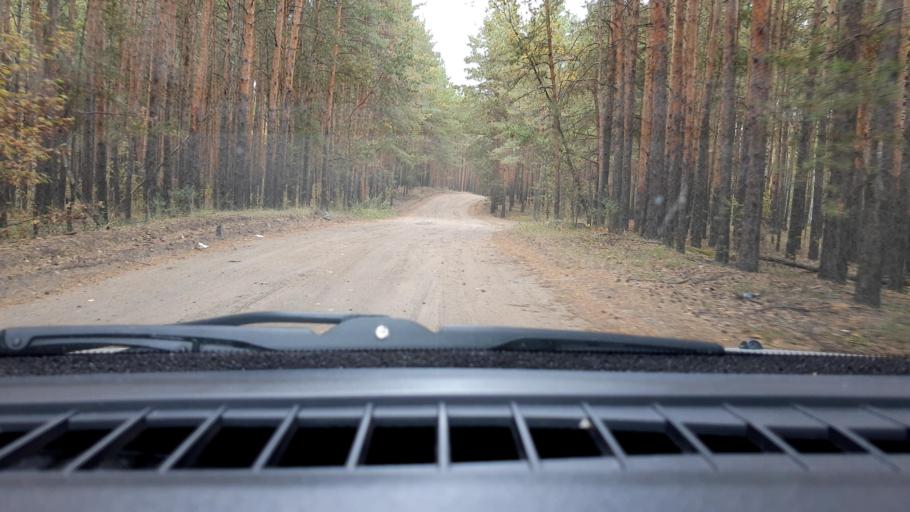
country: RU
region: Nizjnij Novgorod
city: Gorbatovka
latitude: 56.3153
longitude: 43.6960
